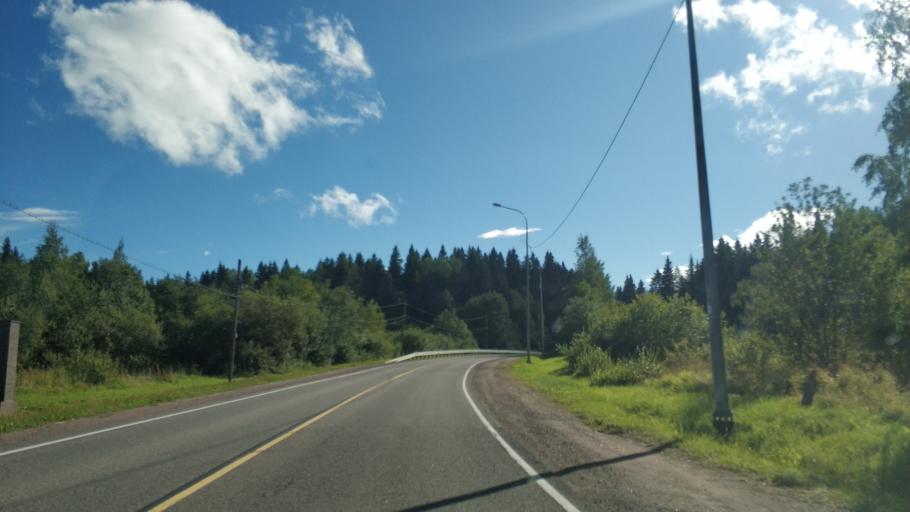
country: RU
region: Republic of Karelia
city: Sortavala
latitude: 61.6584
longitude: 30.6566
